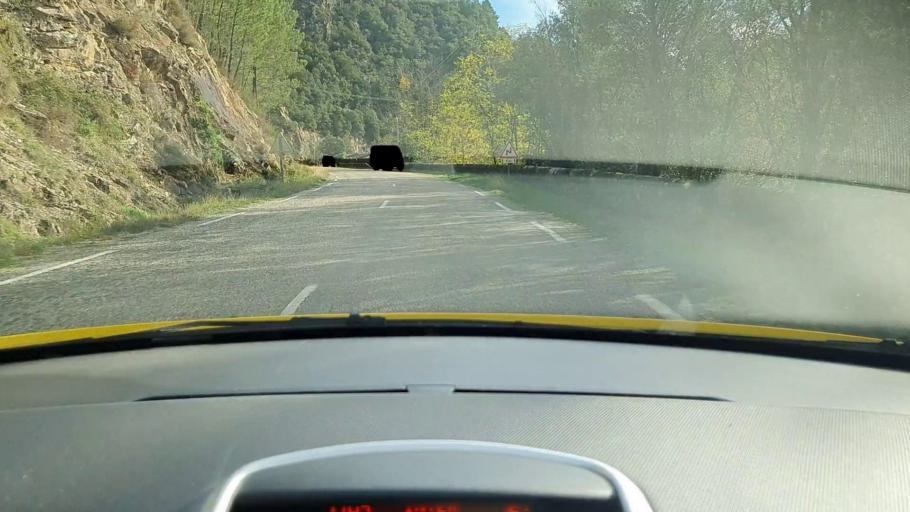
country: FR
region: Languedoc-Roussillon
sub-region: Departement du Gard
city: Lasalle
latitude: 44.1062
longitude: 3.7900
